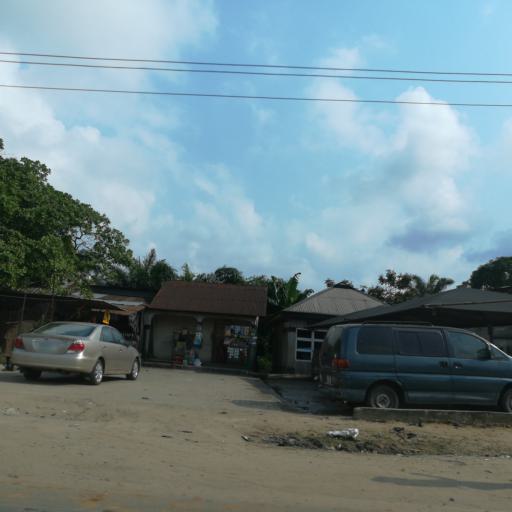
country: NG
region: Rivers
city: Okrika
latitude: 4.7820
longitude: 7.1220
